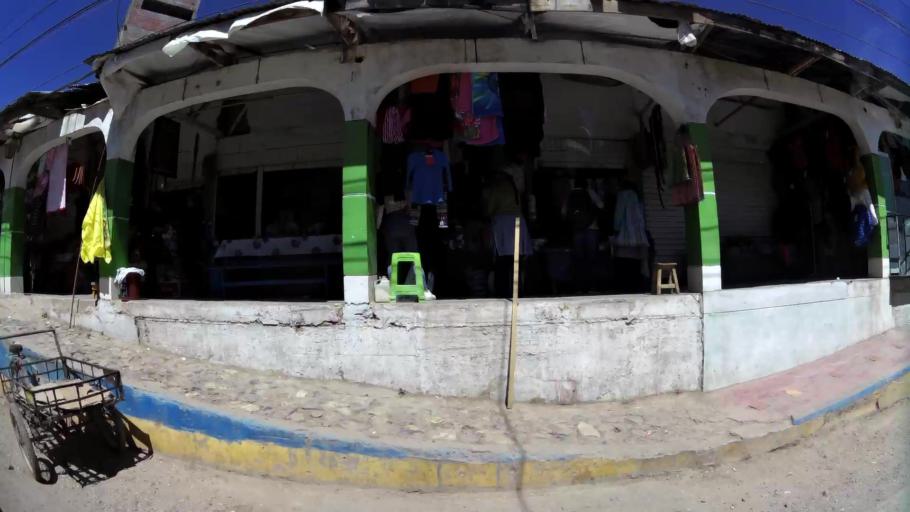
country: PE
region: Junin
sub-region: Provincia de Jauja
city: Jauja
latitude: -11.7784
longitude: -75.4987
